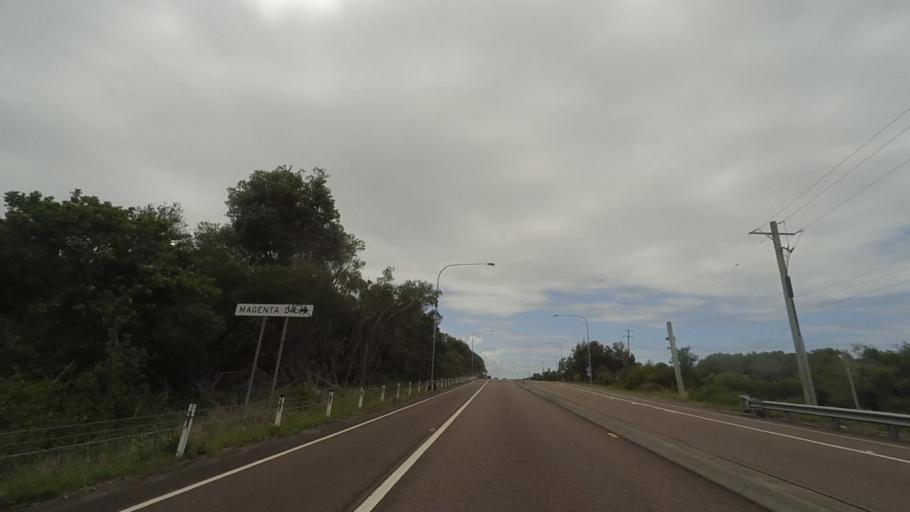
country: AU
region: New South Wales
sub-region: Wyong Shire
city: The Entrance
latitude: -33.3118
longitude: 151.5199
